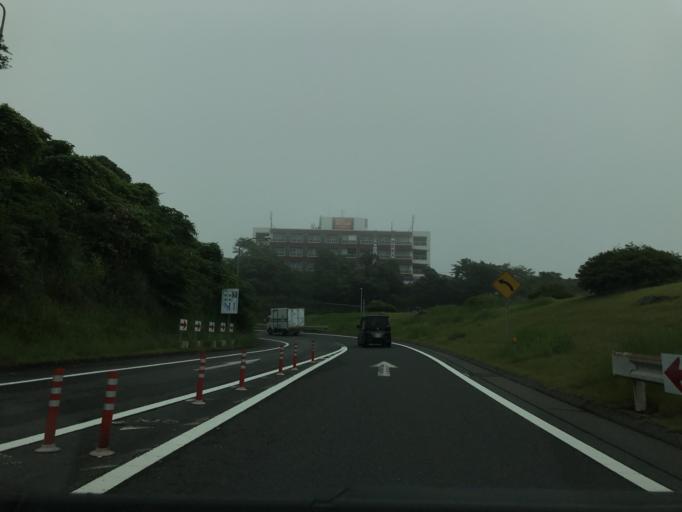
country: JP
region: Oita
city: Beppu
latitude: 33.2944
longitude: 131.4627
